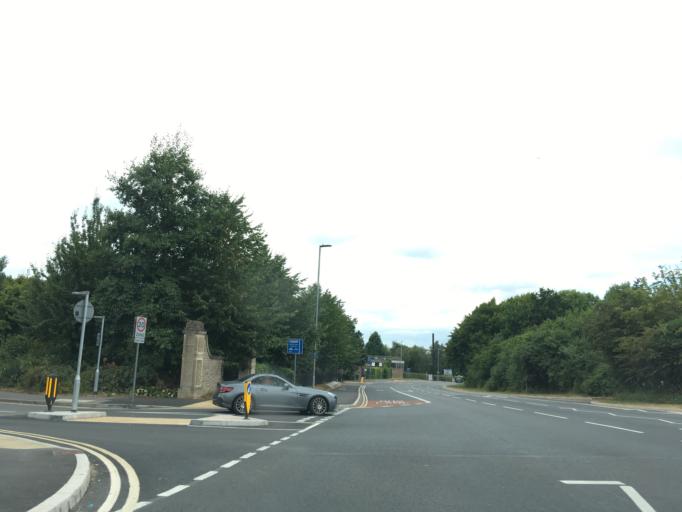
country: GB
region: England
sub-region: South Gloucestershire
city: Stoke Gifford
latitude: 51.4969
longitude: -2.5432
